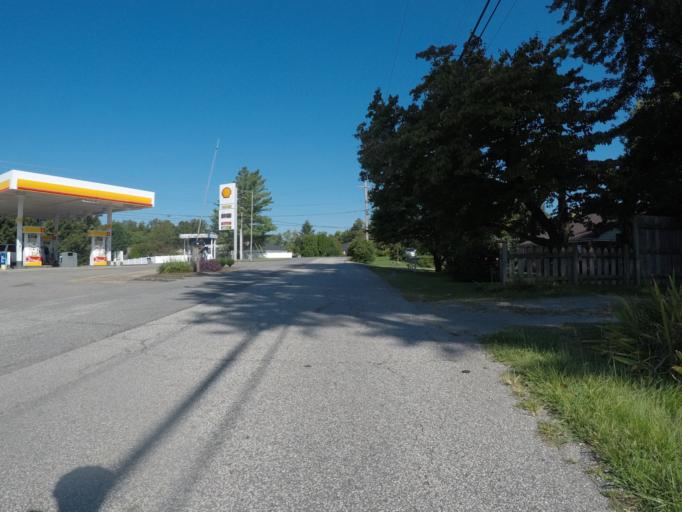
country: US
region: Kentucky
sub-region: Boyd County
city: Westwood
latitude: 38.4881
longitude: -82.6890
